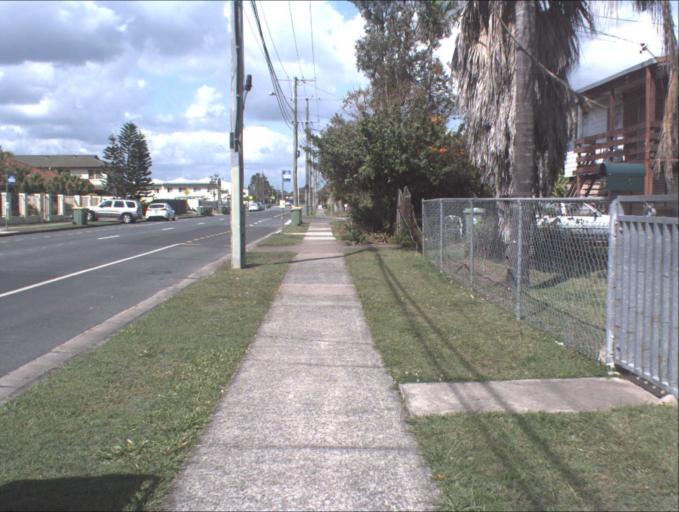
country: AU
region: Queensland
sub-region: Logan
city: Waterford West
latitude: -27.6884
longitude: 153.1345
